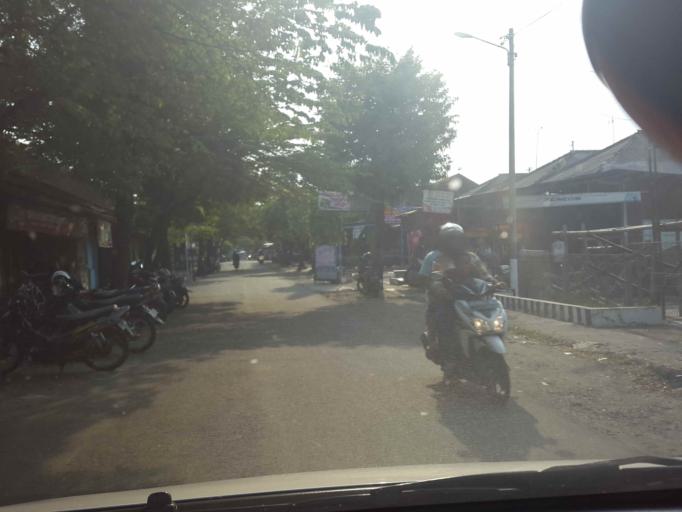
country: ID
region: Central Java
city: Sragen
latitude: -7.4283
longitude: 111.0230
